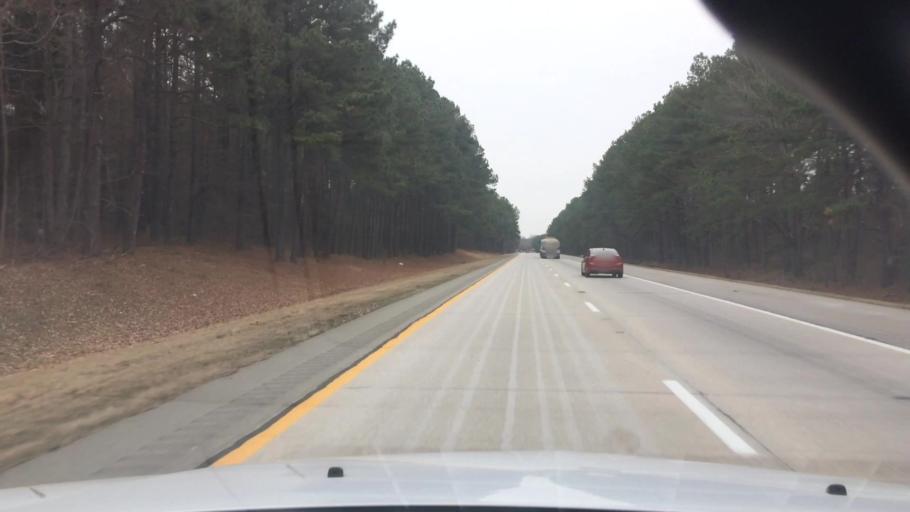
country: US
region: North Carolina
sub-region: Nash County
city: Nashville
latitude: 35.8853
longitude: -77.9427
